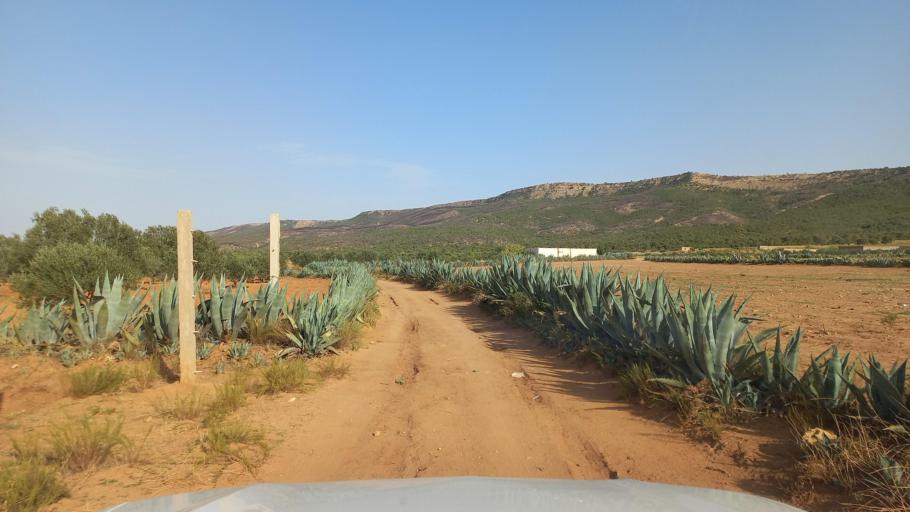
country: TN
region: Al Qasrayn
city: Kasserine
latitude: 35.3426
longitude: 8.8462
